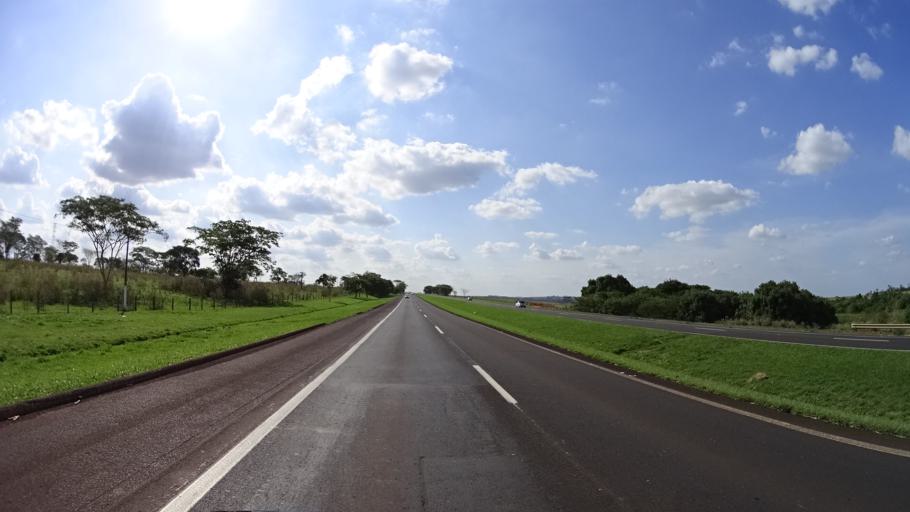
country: BR
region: Sao Paulo
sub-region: Guapiacu
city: Guapiacu
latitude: -20.9771
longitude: -49.2232
